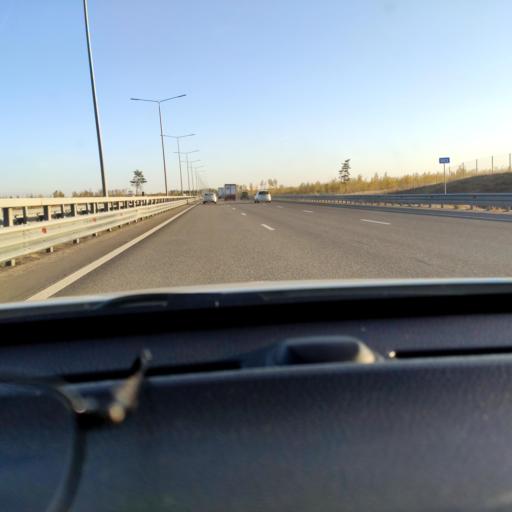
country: RU
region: Voronezj
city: Somovo
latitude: 51.7715
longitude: 39.3018
